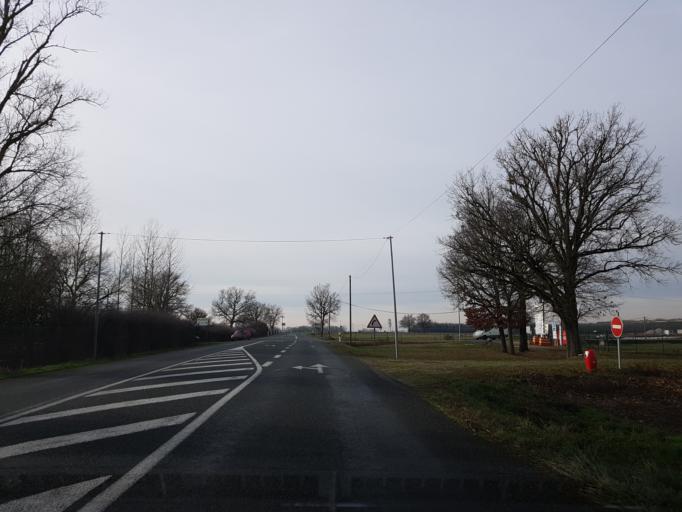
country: FR
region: Auvergne
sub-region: Departement de l'Allier
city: Yzeure
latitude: 46.5778
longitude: 3.4100
